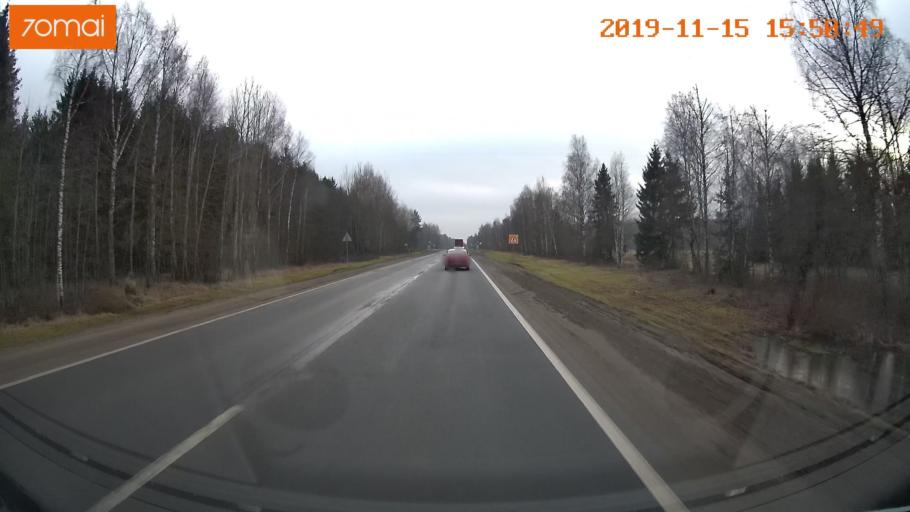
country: RU
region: Jaroslavl
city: Yaroslavl
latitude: 57.9016
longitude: 40.0119
